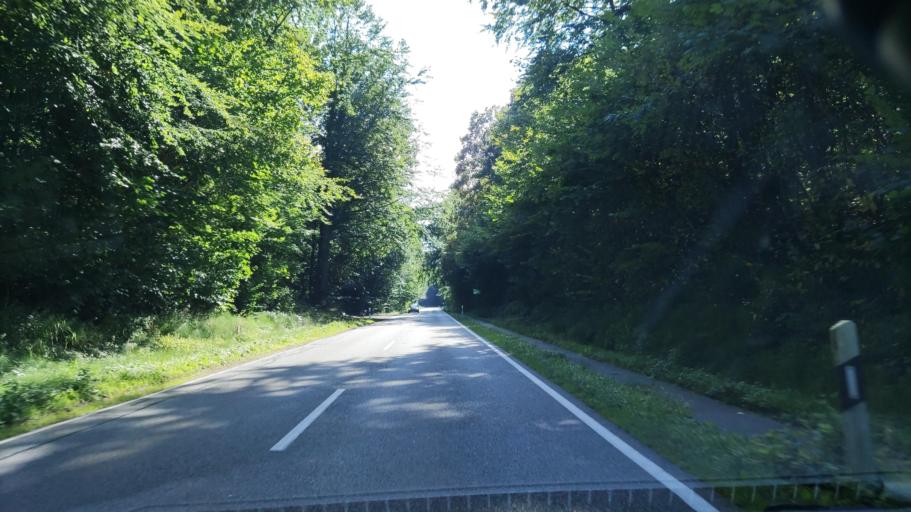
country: DE
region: Schleswig-Holstein
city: Ascheffel
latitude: 54.4272
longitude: 9.7052
